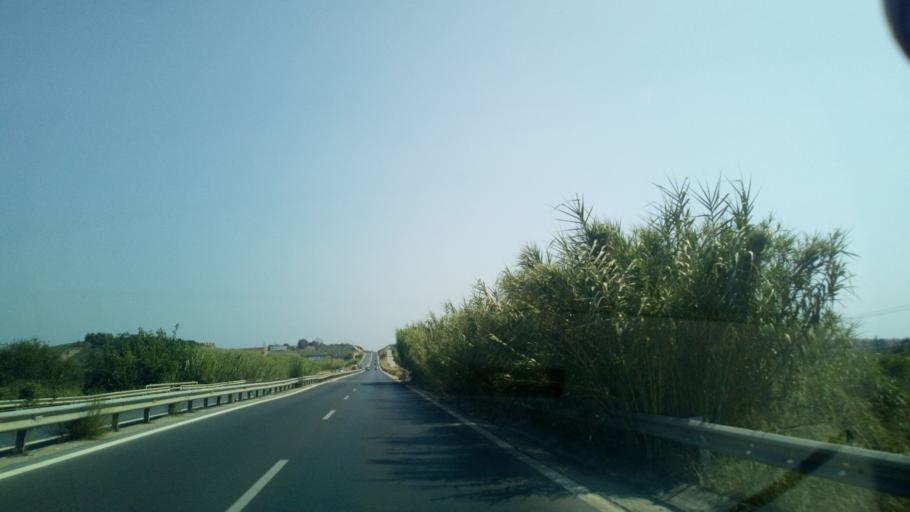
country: GR
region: Central Macedonia
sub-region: Nomos Chalkidikis
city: Nea Moudhania
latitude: 40.2554
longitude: 23.2876
